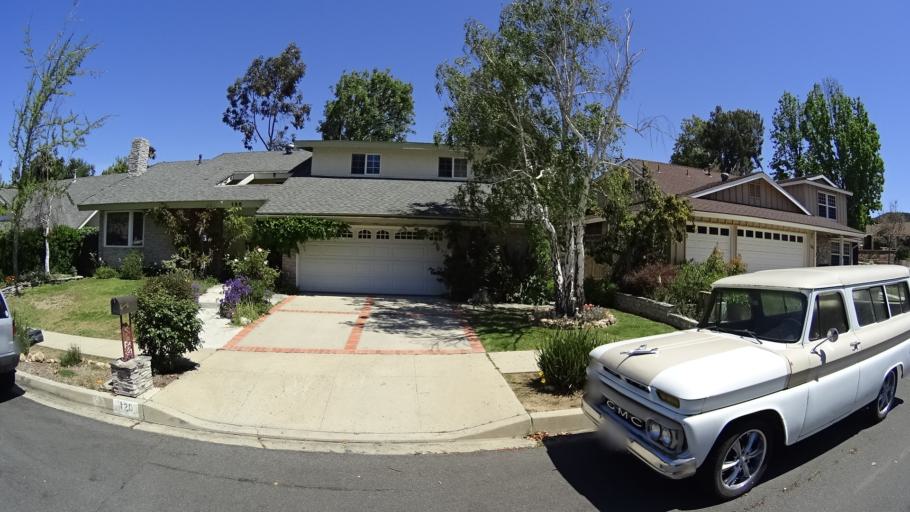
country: US
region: California
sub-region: Ventura County
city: Casa Conejo
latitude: 34.1797
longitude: -118.8987
